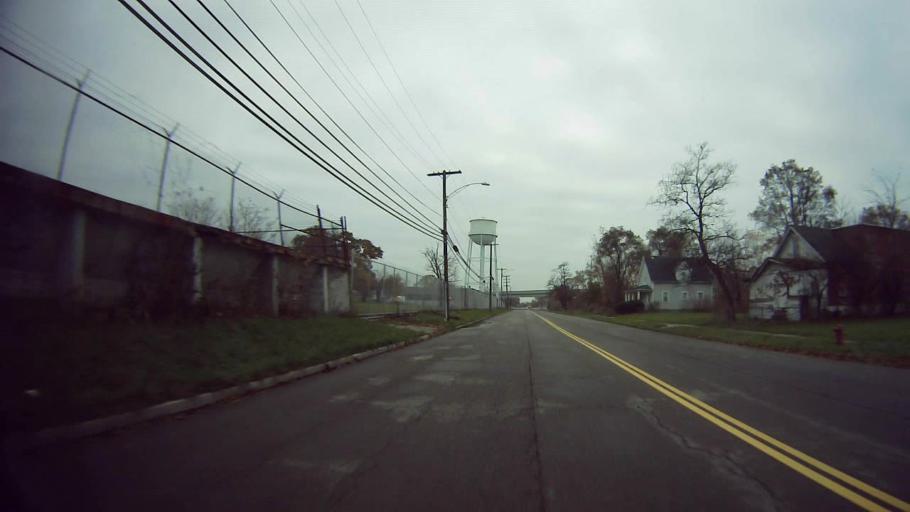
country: US
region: Michigan
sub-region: Wayne County
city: Highland Park
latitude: 42.4114
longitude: -83.0786
